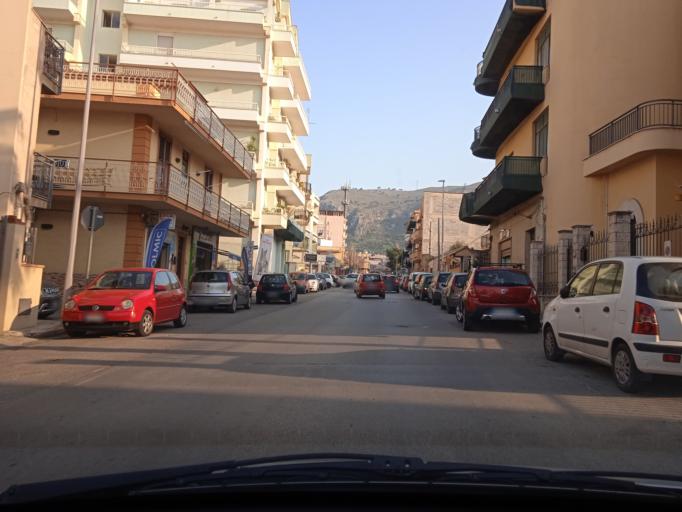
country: IT
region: Sicily
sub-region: Palermo
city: Villabate
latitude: 38.0789
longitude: 13.4374
